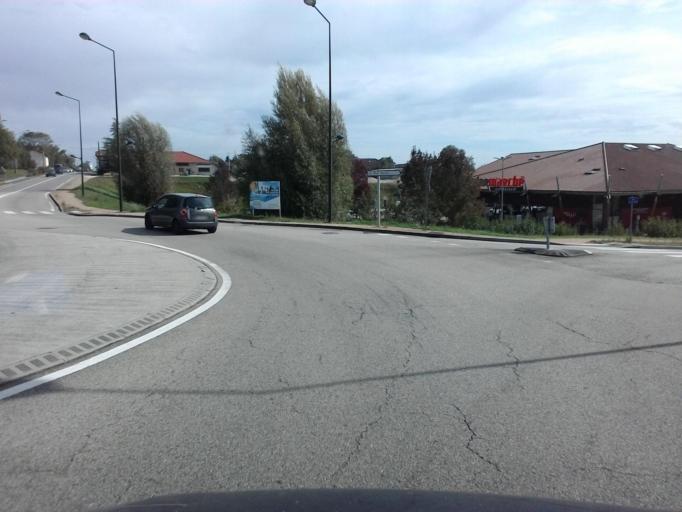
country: FR
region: Rhone-Alpes
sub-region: Departement de l'Ain
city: Polliat
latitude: 46.2486
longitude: 5.1314
